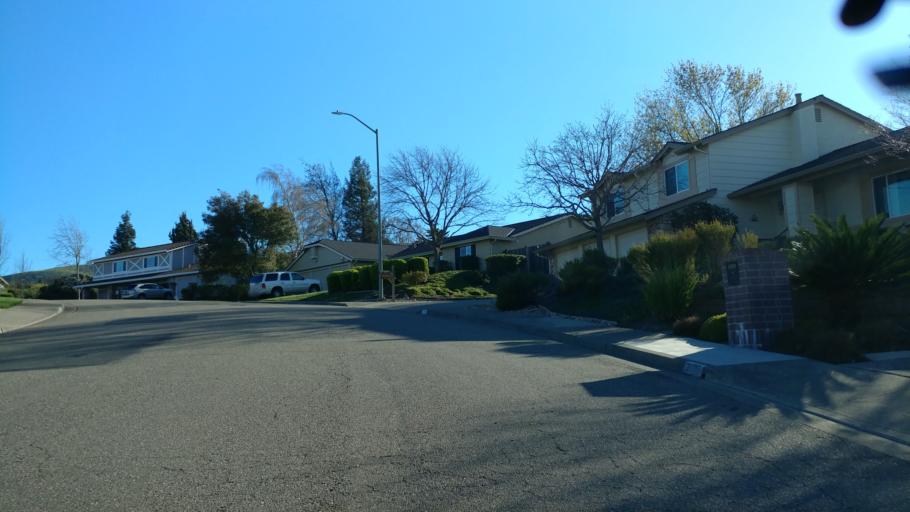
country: US
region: California
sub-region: Contra Costa County
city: San Ramon
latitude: 37.7577
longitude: -121.9835
